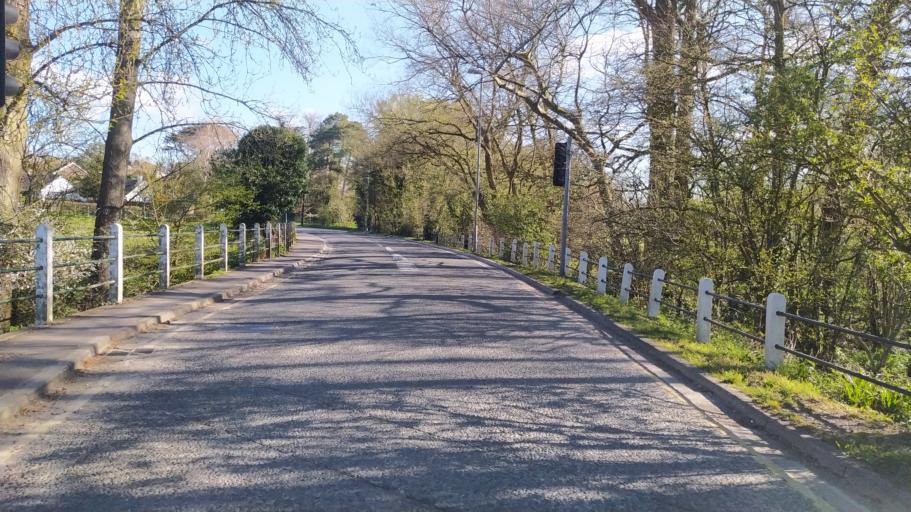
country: GB
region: England
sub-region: Dorset
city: Sturminster Newton
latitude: 50.9220
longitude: -2.3075
